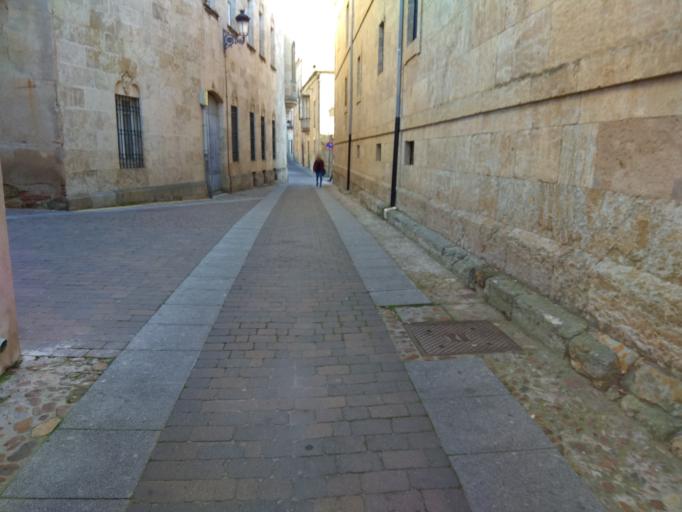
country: ES
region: Castille and Leon
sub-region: Provincia de Salamanca
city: Ciudad Rodrigo
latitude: 40.5984
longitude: -6.5367
